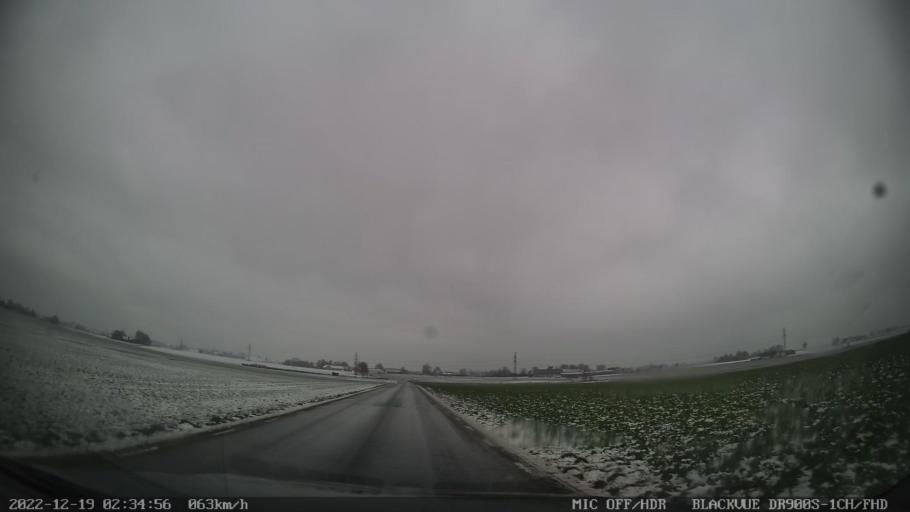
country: SE
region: Skane
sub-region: Tomelilla Kommun
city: Tomelilla
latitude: 55.5378
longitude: 14.0419
